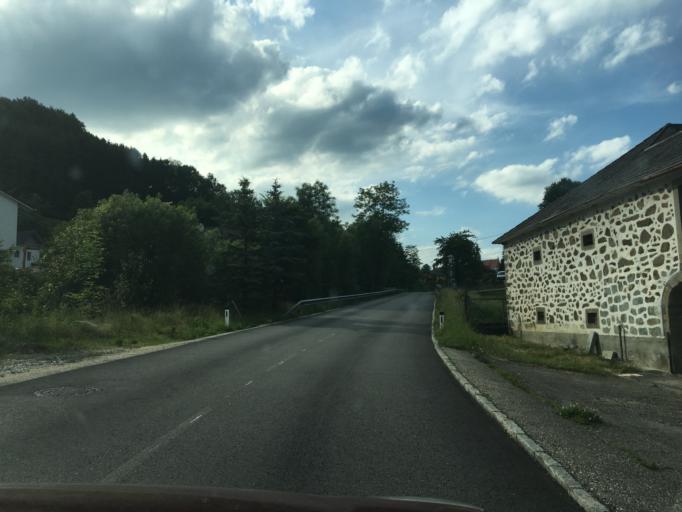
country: AT
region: Upper Austria
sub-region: Politischer Bezirk Urfahr-Umgebung
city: Reichenau im Muhlkreis
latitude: 48.4498
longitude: 14.3543
